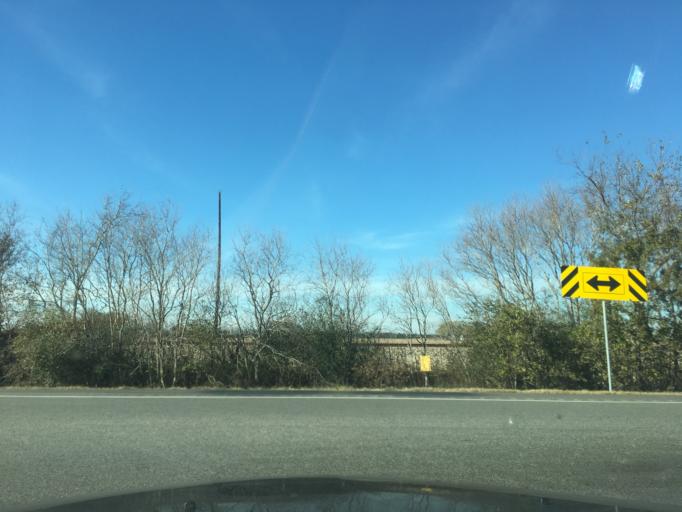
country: US
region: Texas
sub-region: Fort Bend County
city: Pleak
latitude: 29.4853
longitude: -95.9375
